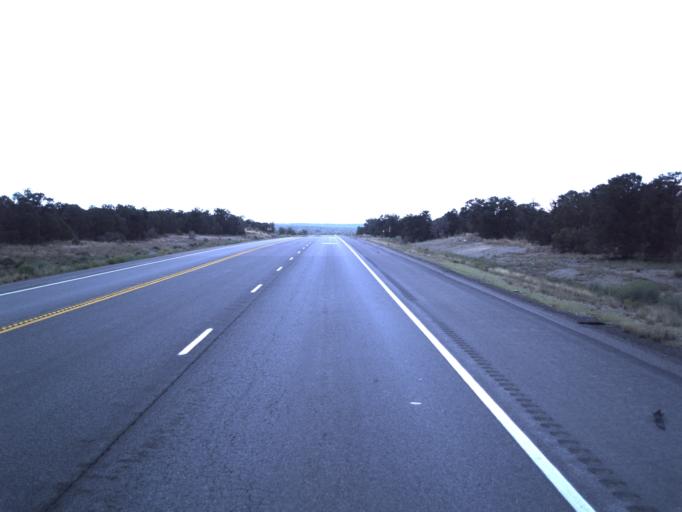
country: US
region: Utah
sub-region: Duchesne County
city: Duchesne
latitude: 40.1815
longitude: -110.6450
